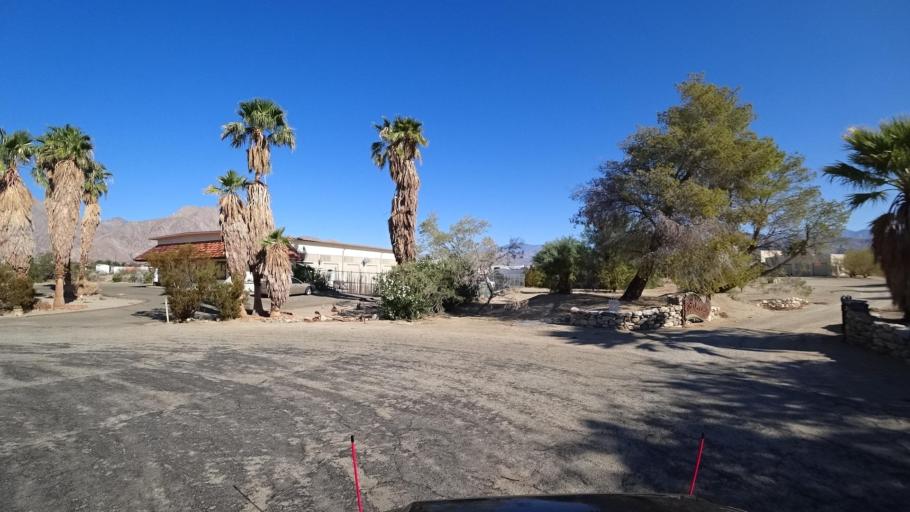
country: US
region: California
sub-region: San Diego County
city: Borrego Springs
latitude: 33.2622
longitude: -116.3712
